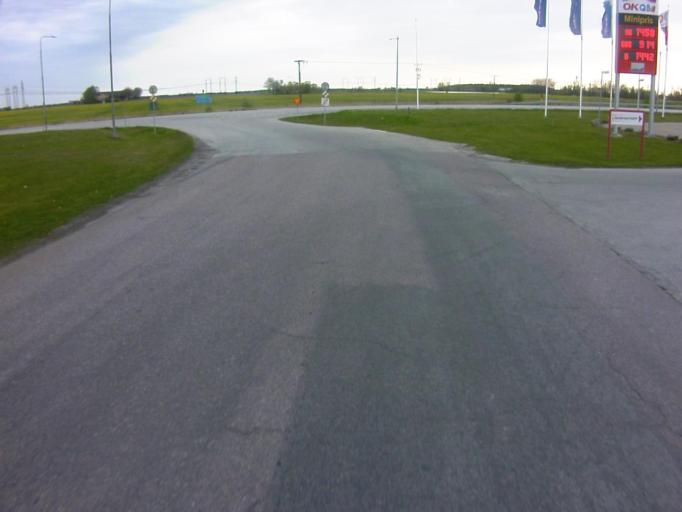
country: SE
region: Skane
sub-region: Kavlinge Kommun
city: Loddekopinge
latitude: 55.7736
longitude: 12.9980
